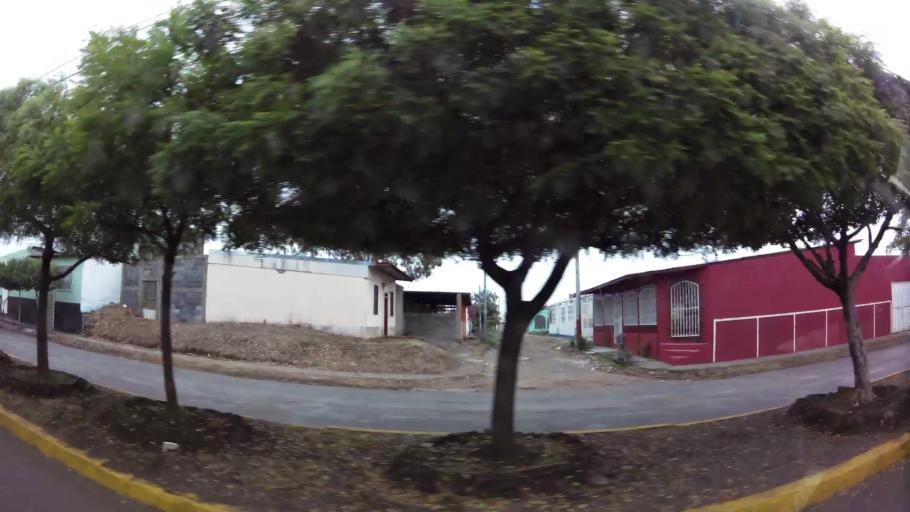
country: NI
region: Granada
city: Granada
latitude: 11.9413
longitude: -85.9504
